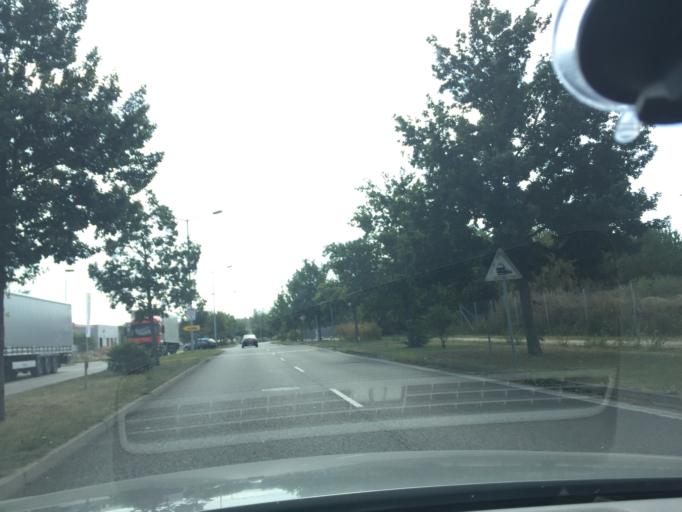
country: DE
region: Brandenburg
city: Grunheide
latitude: 52.3871
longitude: 13.7995
